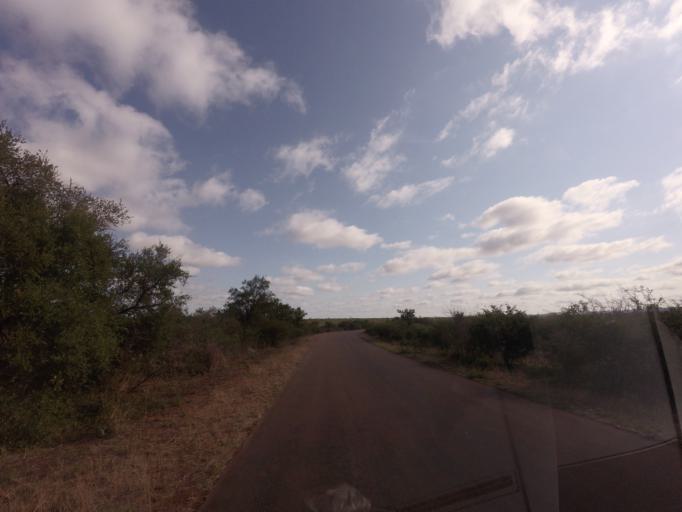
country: ZA
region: Mpumalanga
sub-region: Ehlanzeni District
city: Komatipoort
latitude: -25.1600
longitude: 31.9312
